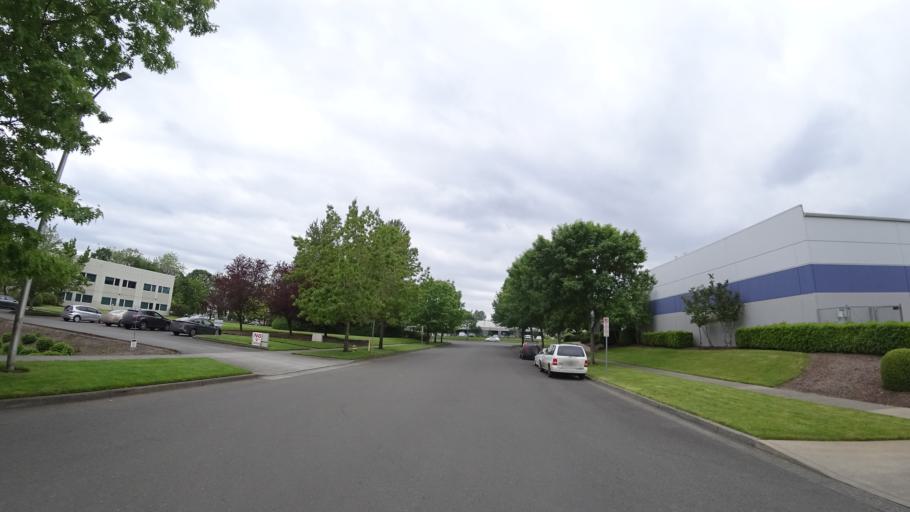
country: US
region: Oregon
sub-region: Washington County
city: Raleigh Hills
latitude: 45.4789
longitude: -122.7773
